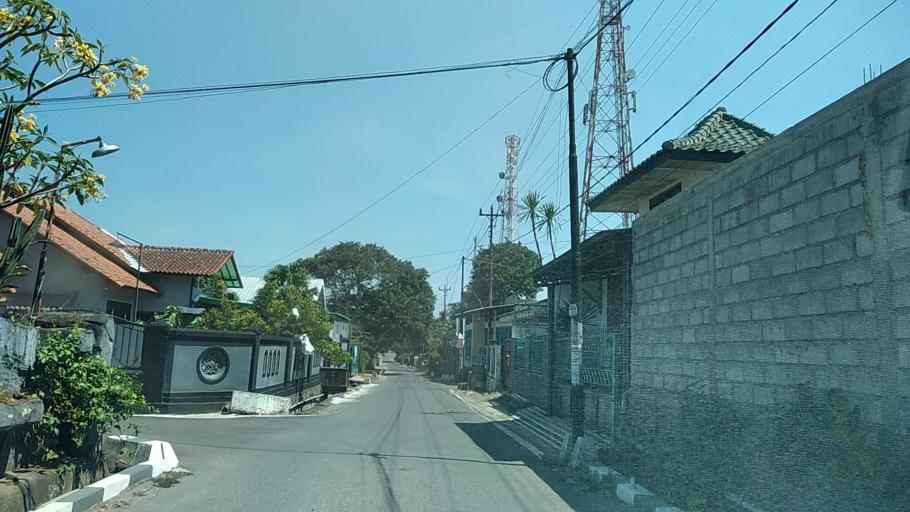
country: ID
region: Central Java
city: Ungaran
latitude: -7.1065
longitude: 110.4125
